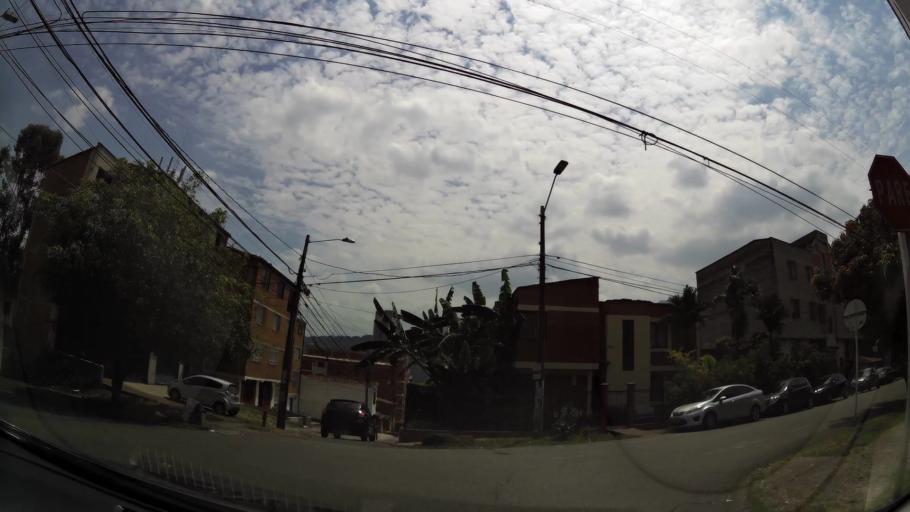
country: CO
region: Antioquia
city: Bello
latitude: 6.3146
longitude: -75.5625
